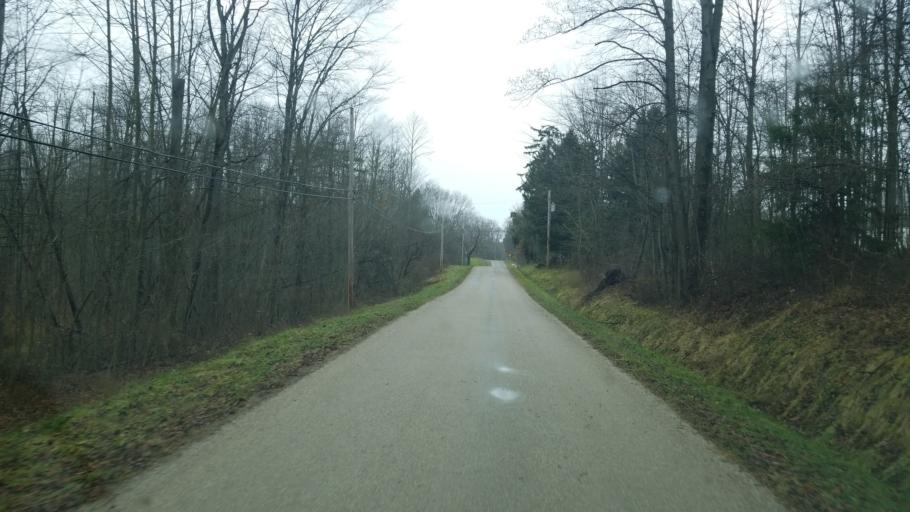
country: US
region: Ohio
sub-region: Ashtabula County
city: Geneva
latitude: 41.7572
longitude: -80.8795
